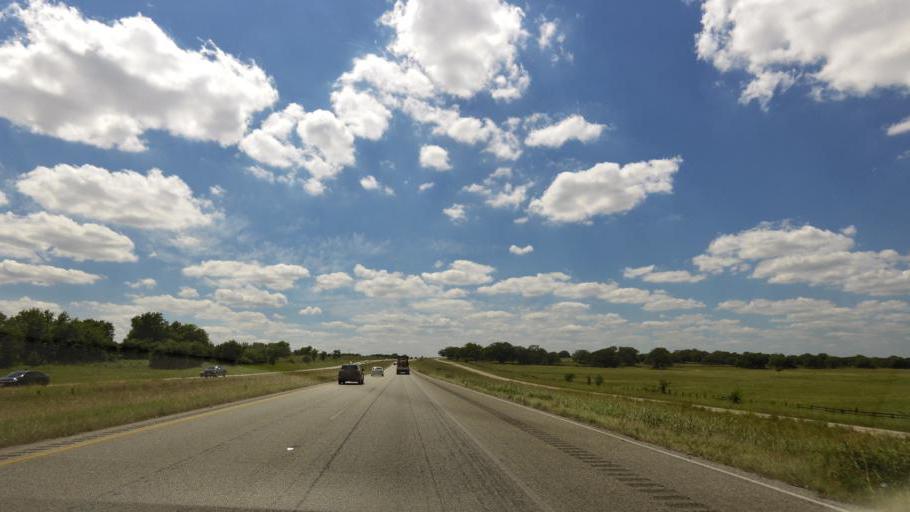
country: US
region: Texas
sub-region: Fayette County
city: Schulenburg
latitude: 29.6892
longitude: -96.9500
